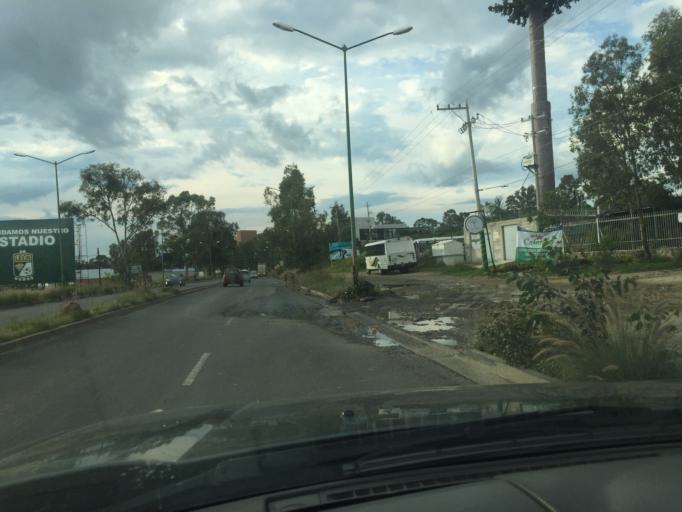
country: MX
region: Guanajuato
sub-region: Leon
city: La Ermita
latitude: 21.1656
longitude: -101.7279
